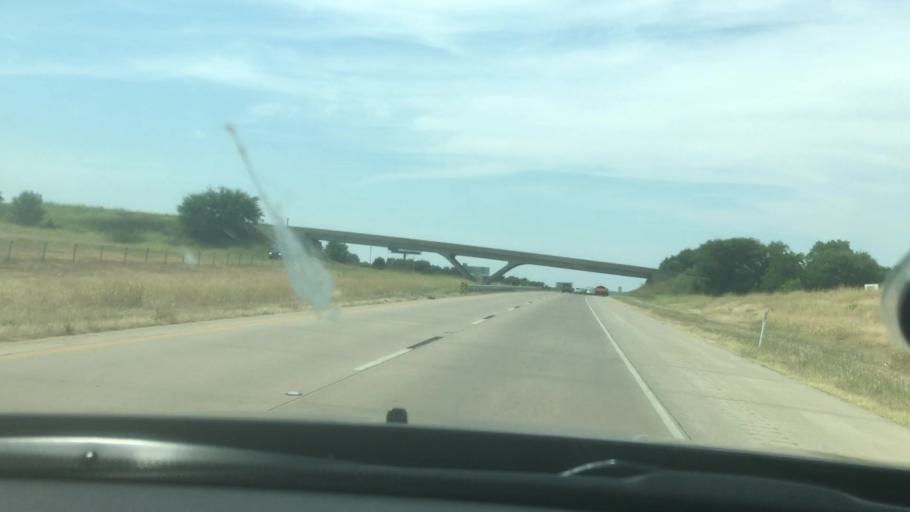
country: US
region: Oklahoma
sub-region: Carter County
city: Ardmore
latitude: 34.3199
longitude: -97.1562
